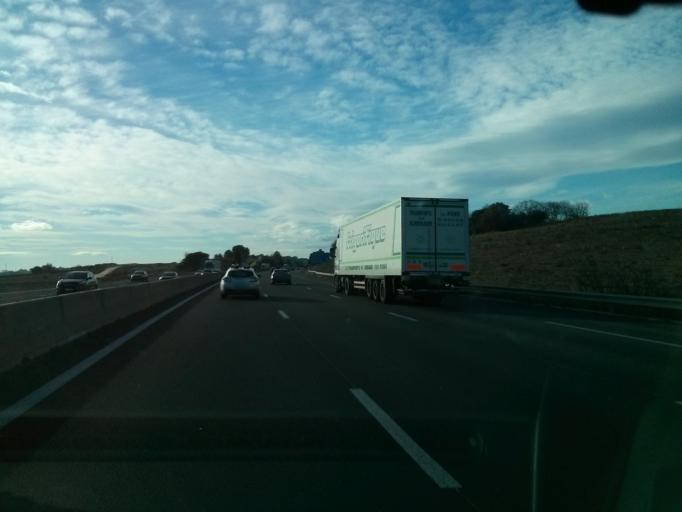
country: FR
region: Languedoc-Roussillon
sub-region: Departement de l'Herault
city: Lunel-Viel
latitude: 43.6982
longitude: 4.1073
